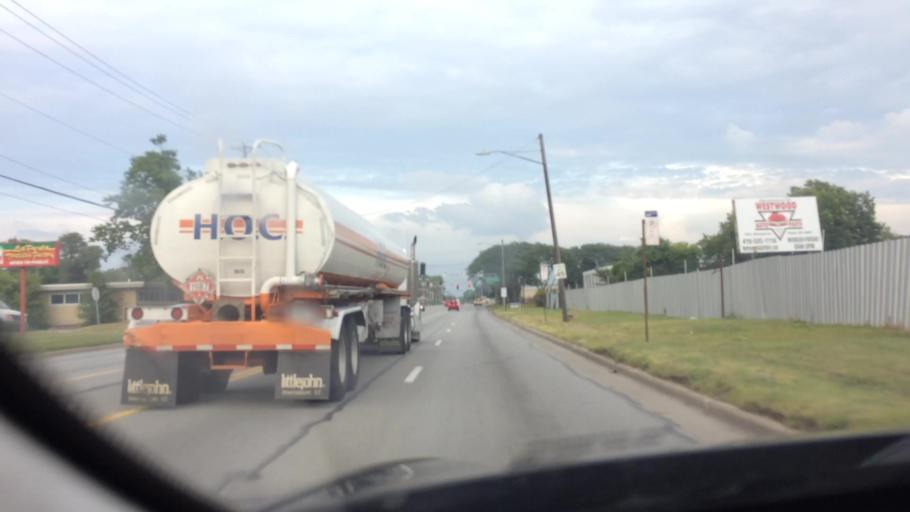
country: US
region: Ohio
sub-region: Lucas County
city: Ottawa Hills
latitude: 41.6380
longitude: -83.6097
